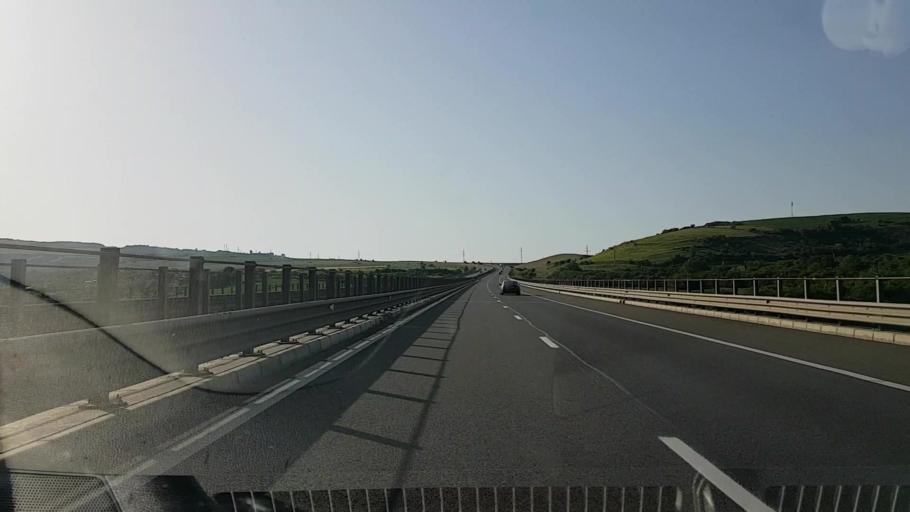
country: RO
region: Cluj
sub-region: Comuna Sandulesti
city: Copaceni
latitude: 46.5758
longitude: 23.7440
